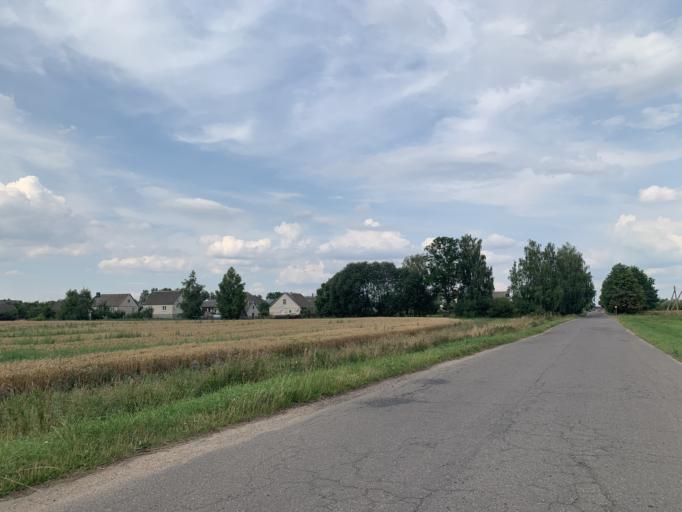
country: BY
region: Minsk
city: Nyasvizh
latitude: 53.2048
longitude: 26.6809
